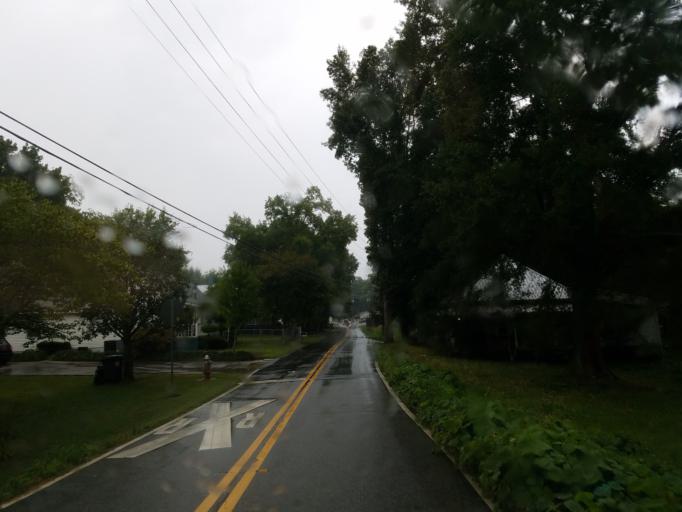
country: US
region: Georgia
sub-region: Bartow County
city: Rydal
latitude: 34.2805
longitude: -84.7477
